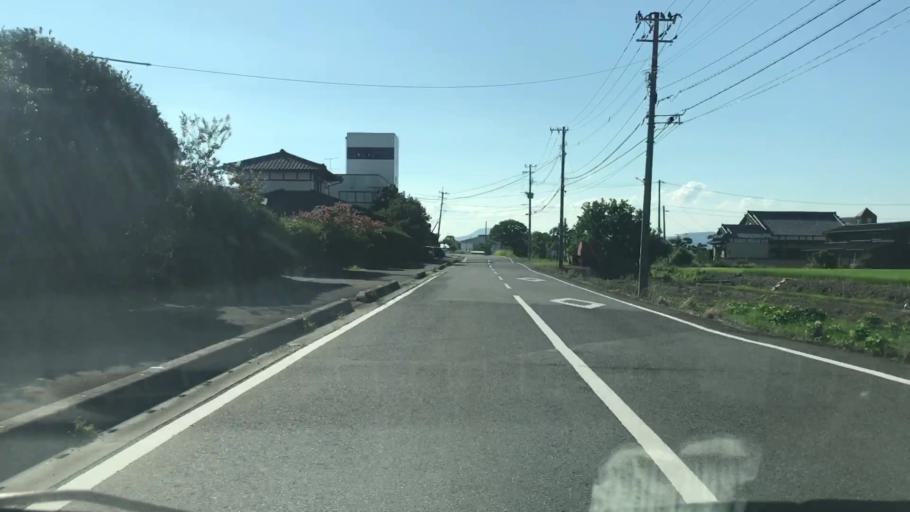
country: JP
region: Saga Prefecture
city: Saga-shi
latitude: 33.1904
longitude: 130.2861
